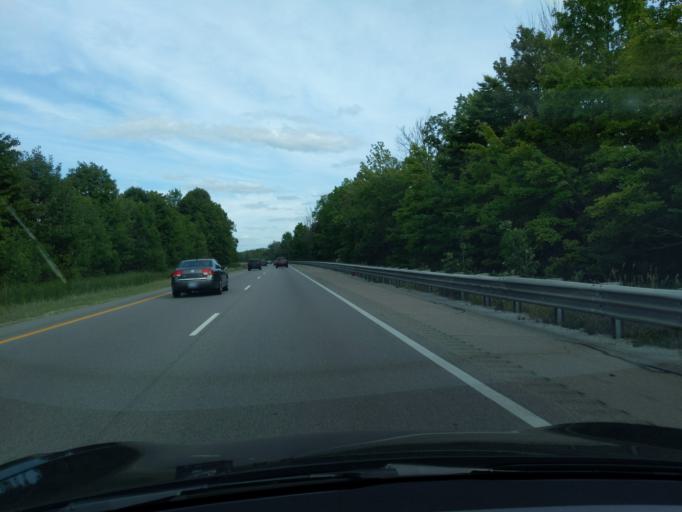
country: US
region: Michigan
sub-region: Ottawa County
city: Coopersville
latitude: 43.0711
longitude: -86.0340
